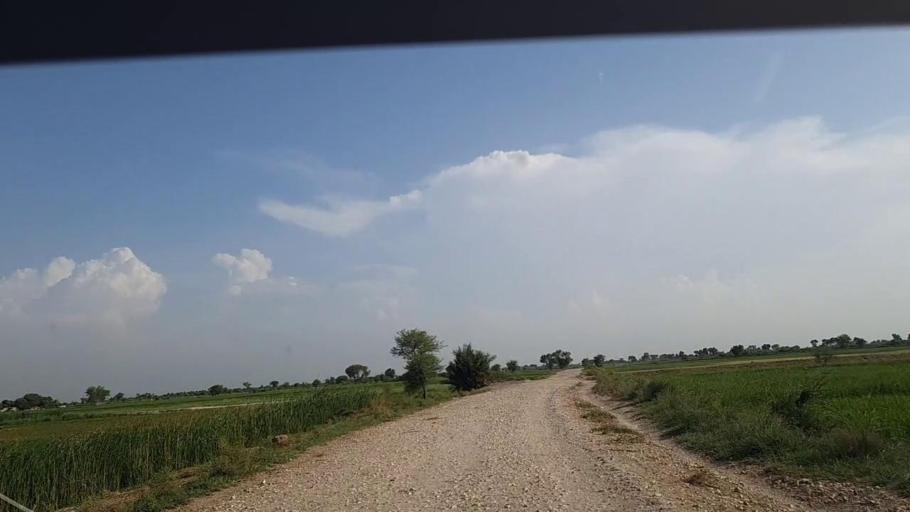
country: PK
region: Sindh
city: Khanpur
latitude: 27.8493
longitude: 69.3778
